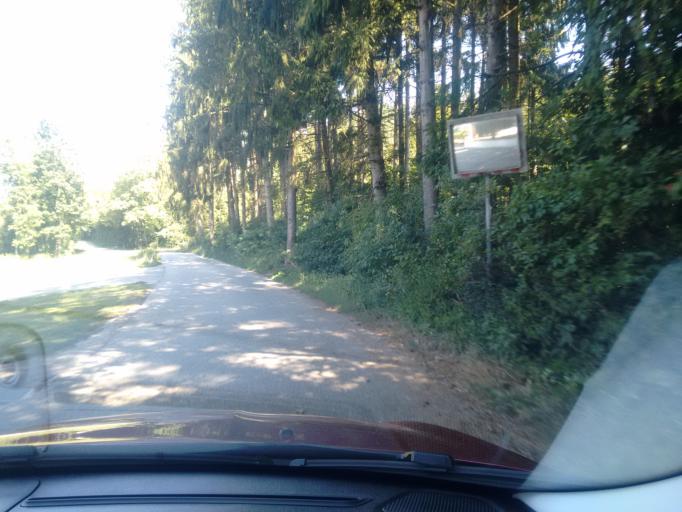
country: AT
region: Upper Austria
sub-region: Wels-Land
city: Steinhaus
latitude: 48.0994
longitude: 14.0458
